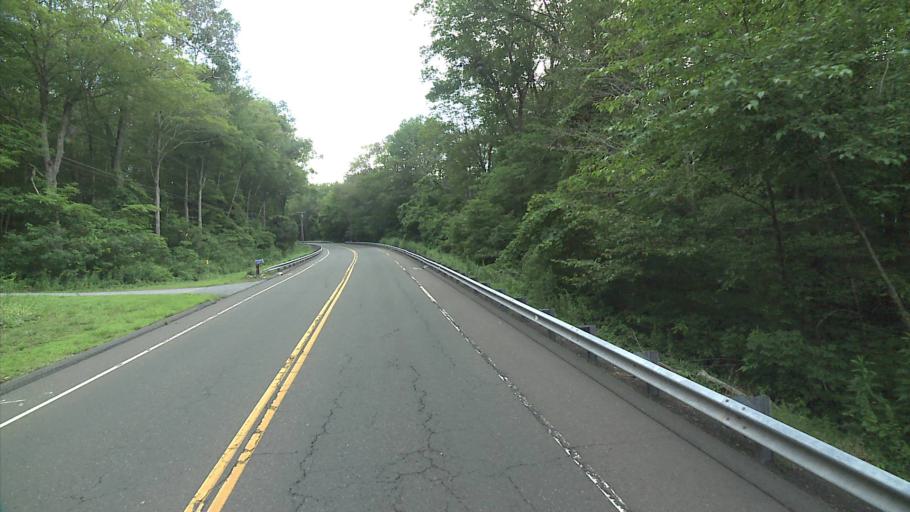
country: US
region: Connecticut
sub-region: Middlesex County
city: Deep River Center
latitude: 41.3501
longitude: -72.4964
